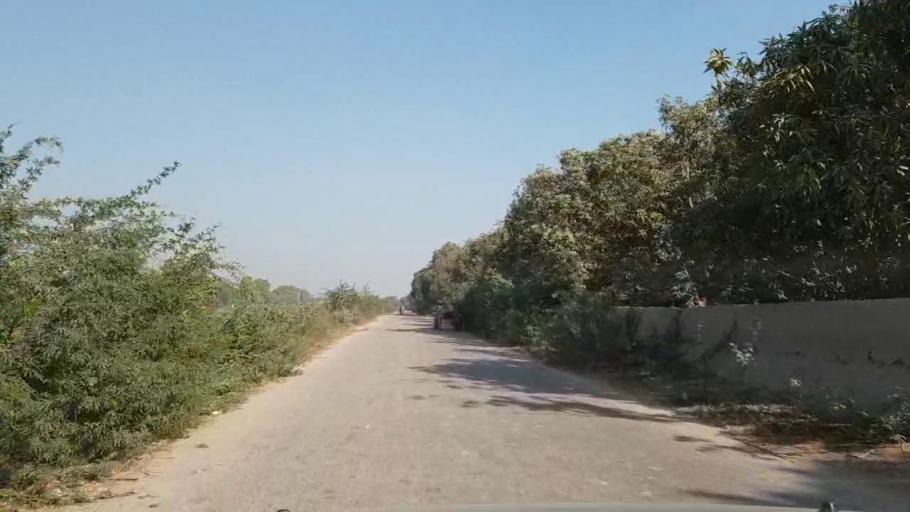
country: PK
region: Sindh
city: Matiari
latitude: 25.6214
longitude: 68.5915
